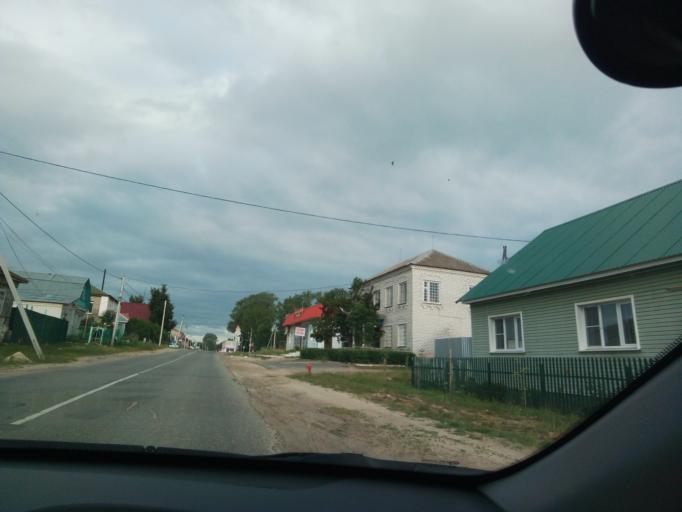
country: RU
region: Rjazan
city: Yermish'
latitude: 54.7704
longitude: 42.2777
